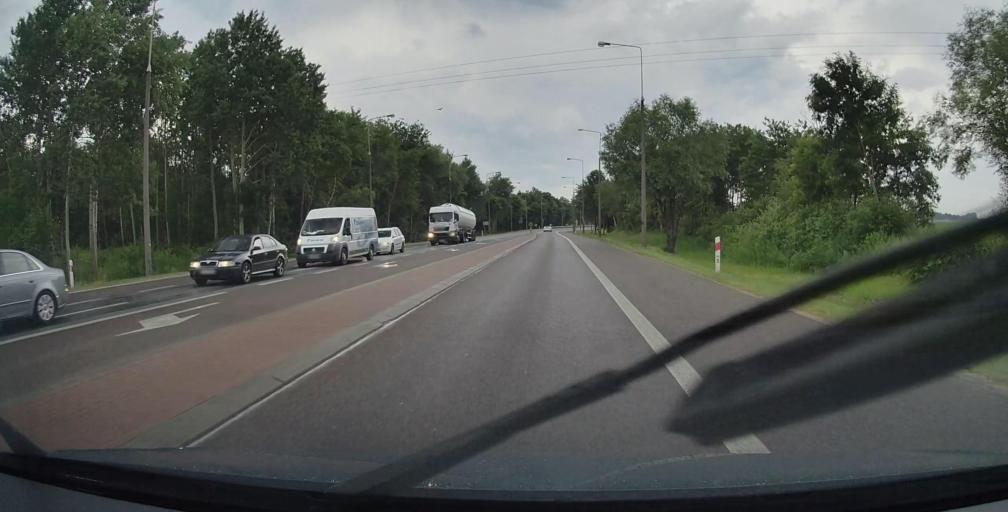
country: PL
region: Lublin Voivodeship
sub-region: Powiat bialski
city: Miedzyrzec Podlaski
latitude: 52.0004
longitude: 22.7632
